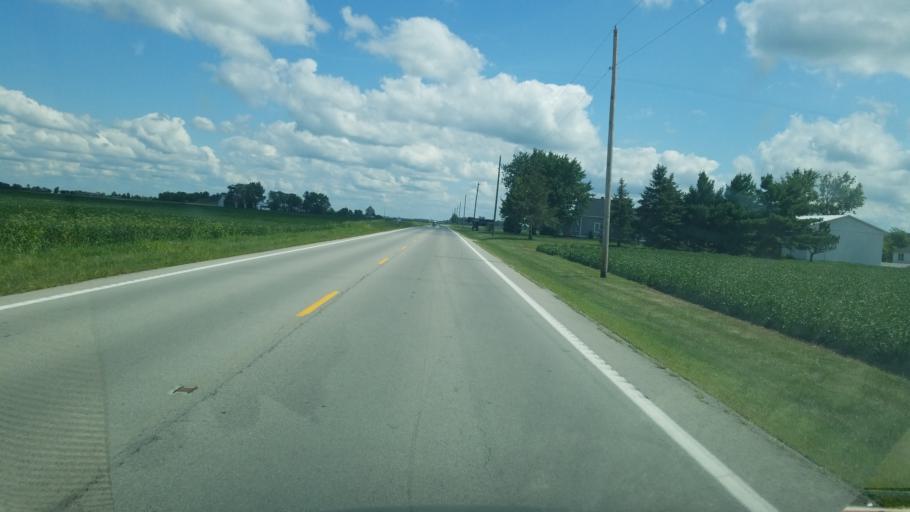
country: US
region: Ohio
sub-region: Putnam County
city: Kalida
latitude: 40.9579
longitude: -84.1772
